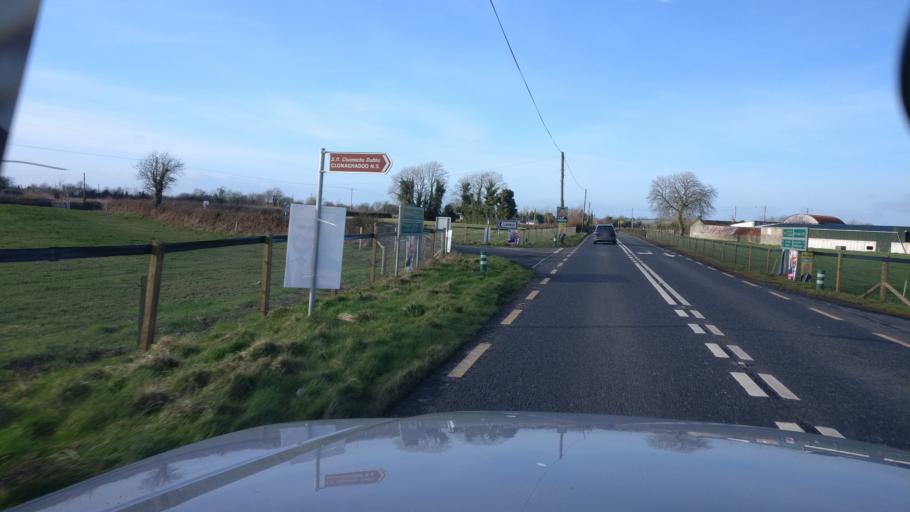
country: IE
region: Leinster
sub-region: Laois
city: Mountmellick
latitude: 53.1697
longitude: -7.3796
